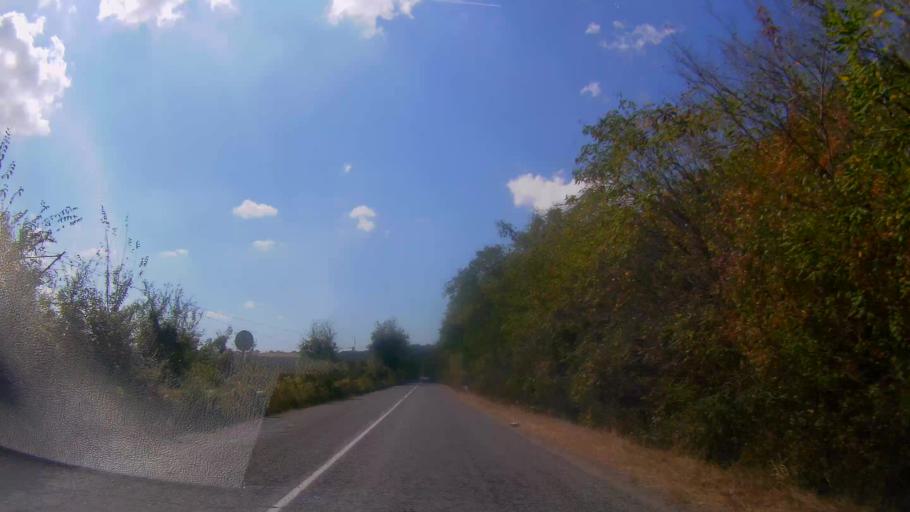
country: BG
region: Veliko Turnovo
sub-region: Obshtina Polski Trumbesh
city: Polski Trumbesh
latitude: 43.4449
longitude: 25.6566
